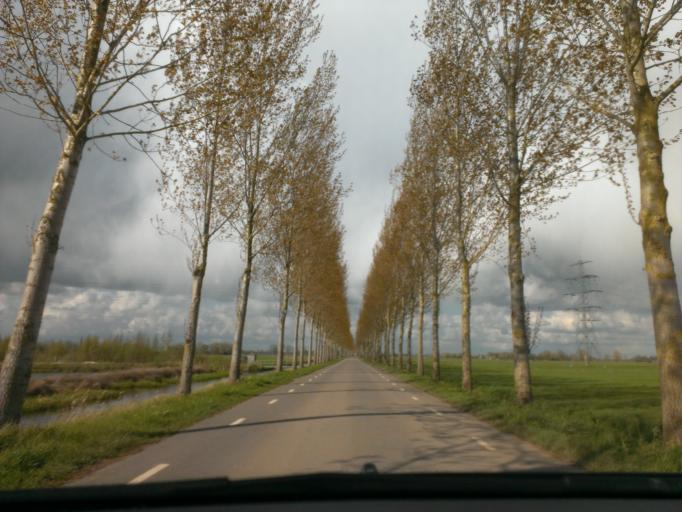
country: NL
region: Gelderland
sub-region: Gemeente Epe
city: Oene
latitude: 52.3104
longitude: 6.0436
